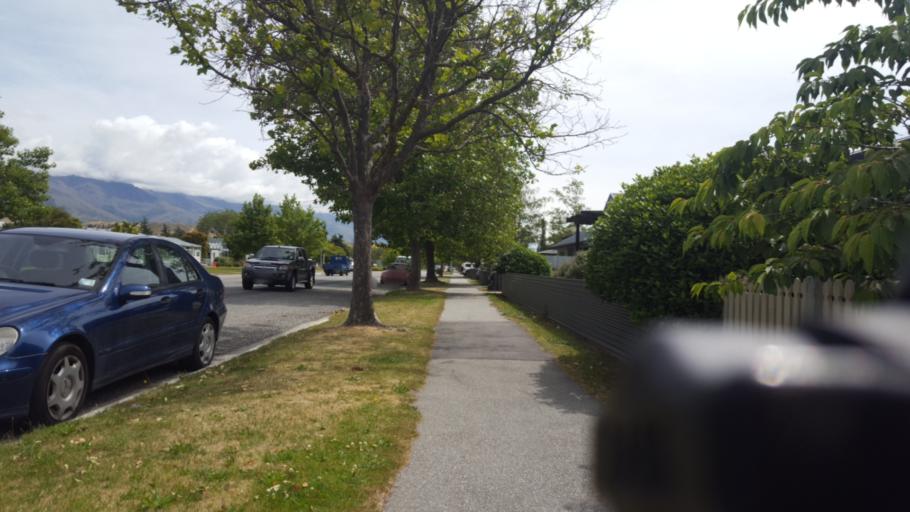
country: NZ
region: Otago
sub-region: Queenstown-Lakes District
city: Wanaka
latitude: -45.0448
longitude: 169.1961
